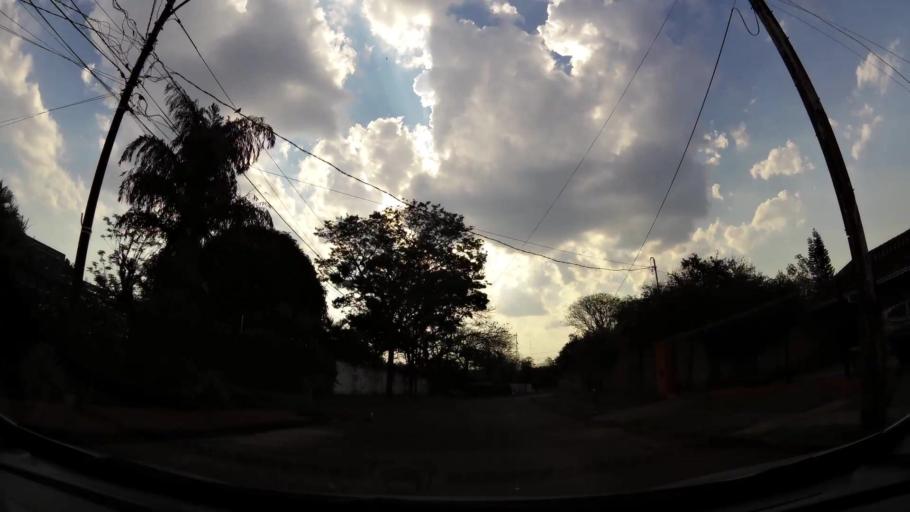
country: PY
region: Alto Parana
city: Presidente Franco
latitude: -25.5205
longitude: -54.6352
